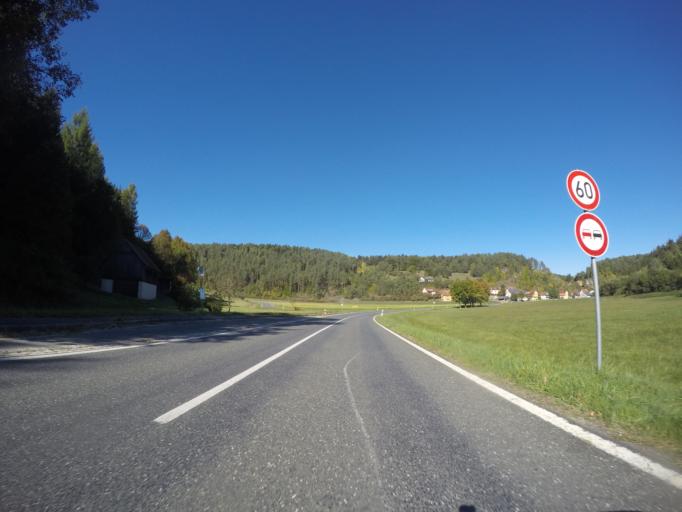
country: DE
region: Bavaria
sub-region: Upper Franconia
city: Waischenfeld
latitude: 49.8087
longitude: 11.3445
